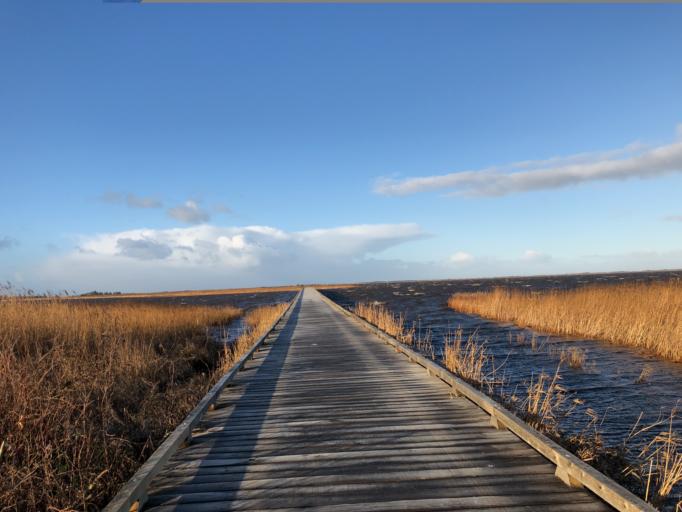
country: DK
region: Central Jutland
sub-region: Ringkobing-Skjern Kommune
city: Ringkobing
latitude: 56.1509
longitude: 8.2399
